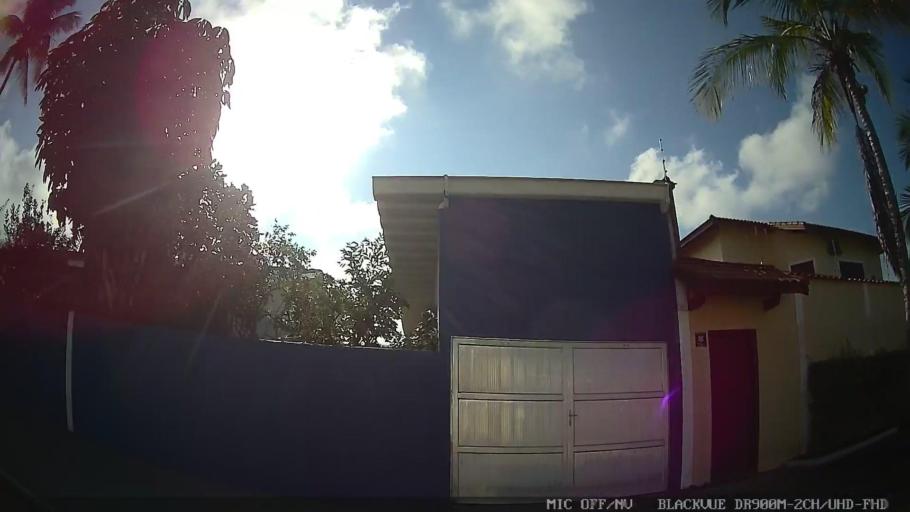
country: BR
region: Sao Paulo
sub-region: Peruibe
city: Peruibe
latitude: -24.2902
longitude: -46.9640
